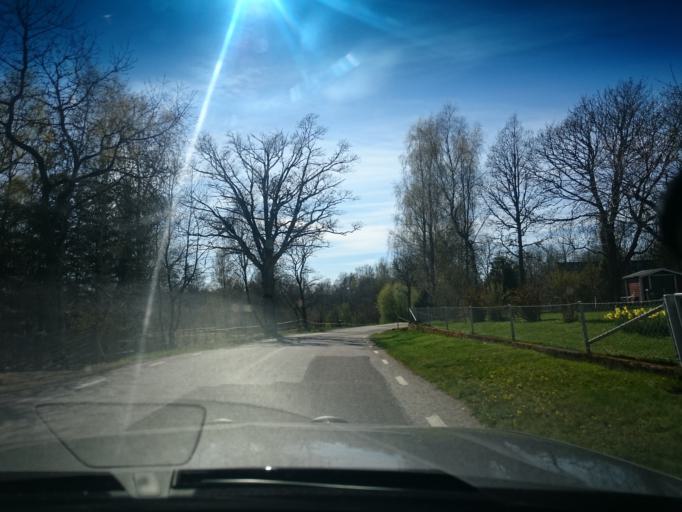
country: SE
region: Kalmar
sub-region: Hultsfreds Kommun
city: Virserum
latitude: 57.3303
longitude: 15.5058
